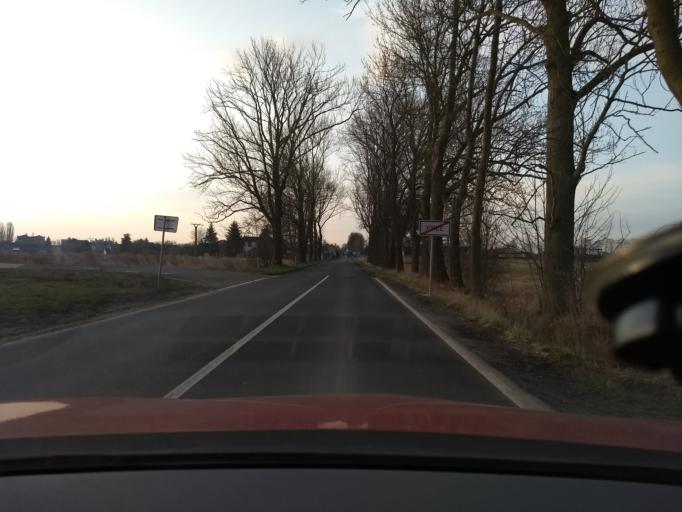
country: CZ
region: Central Bohemia
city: Jenec
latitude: 50.0499
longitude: 14.1799
